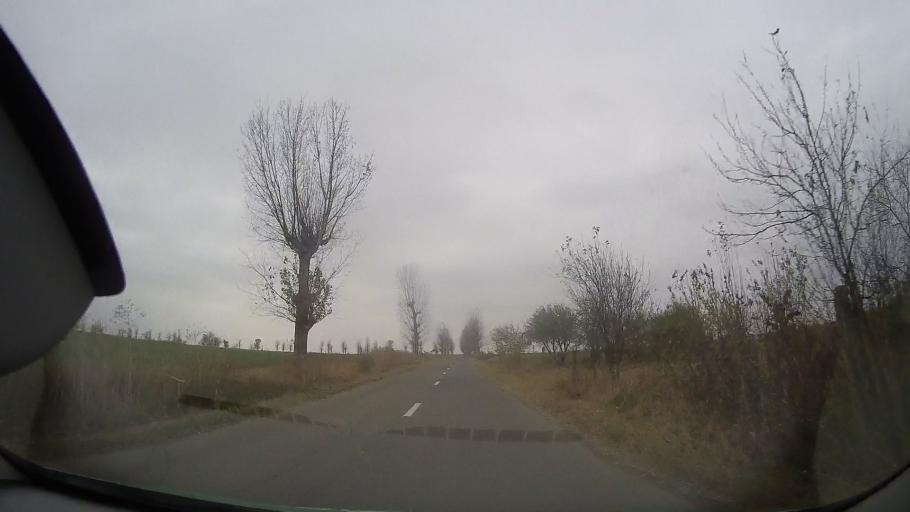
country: RO
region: Ialomita
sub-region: Comuna Grindu
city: Grindu
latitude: 44.7710
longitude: 26.8940
